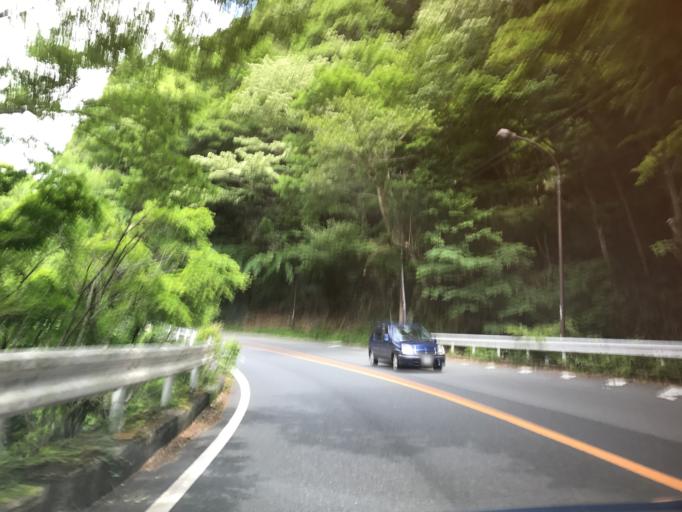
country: JP
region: Kanagawa
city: Hakone
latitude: 35.2619
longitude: 139.0275
